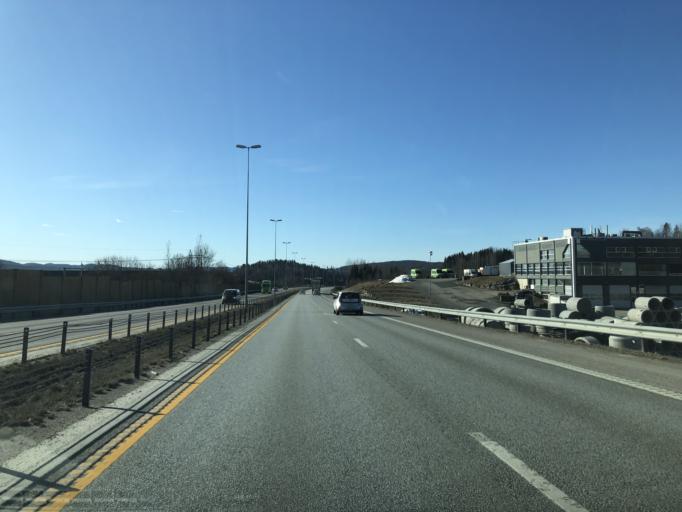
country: NO
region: Akershus
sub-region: Skedsmo
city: Lillestrom
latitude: 59.9921
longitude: 11.0318
